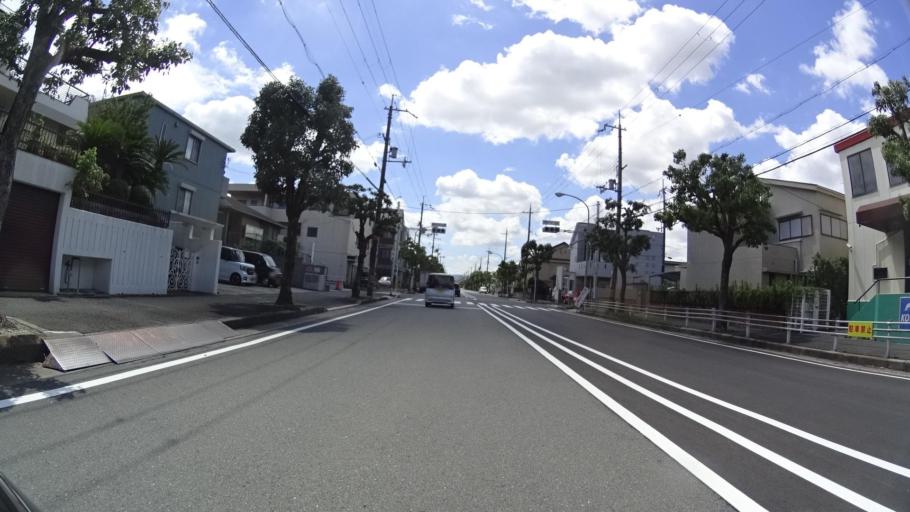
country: JP
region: Kyoto
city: Yawata
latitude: 34.8671
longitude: 135.6924
